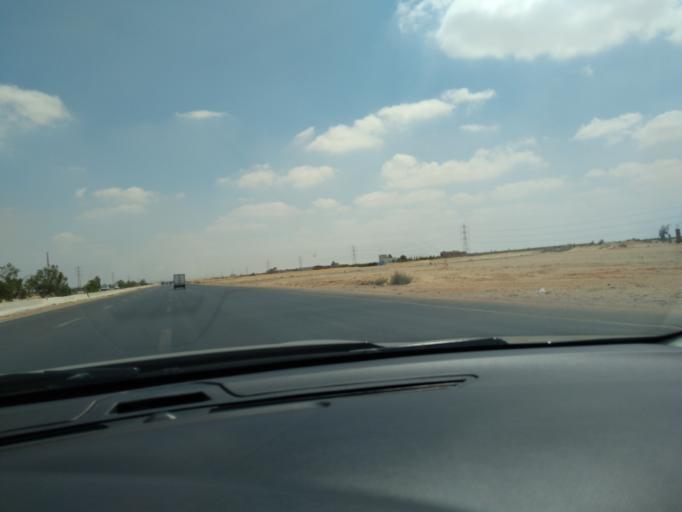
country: EG
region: Al Isma'iliyah
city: At Tall al Kabir
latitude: 30.3495
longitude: 31.8827
